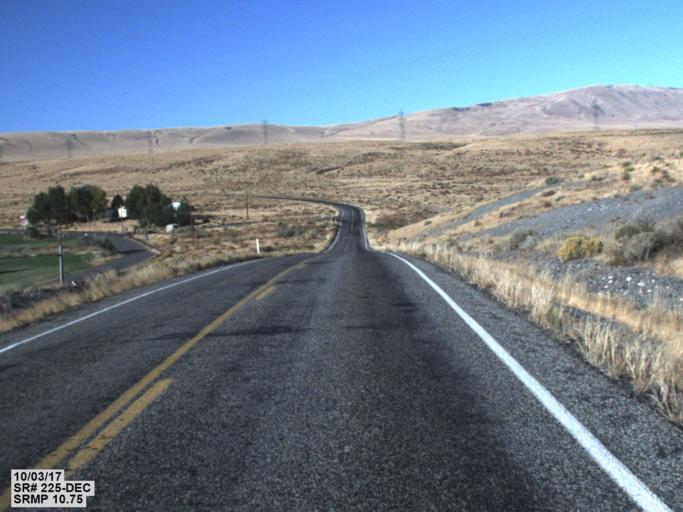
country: US
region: Washington
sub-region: Benton County
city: West Richland
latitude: 46.3819
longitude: -119.4341
